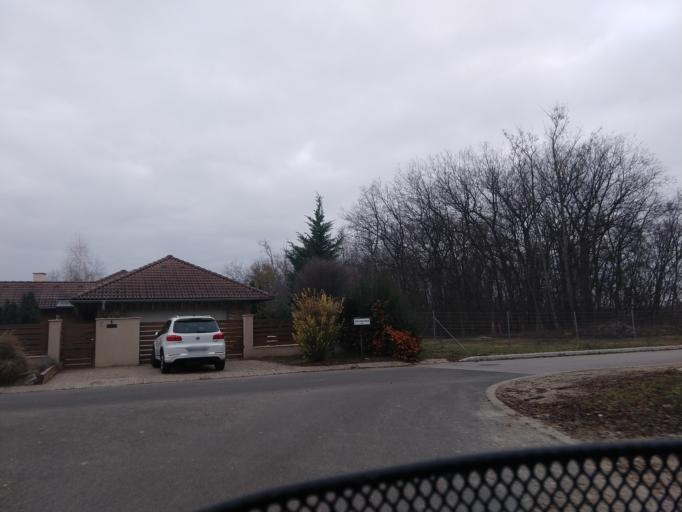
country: HU
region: Pest
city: Orbottyan
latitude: 47.6626
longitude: 19.2562
